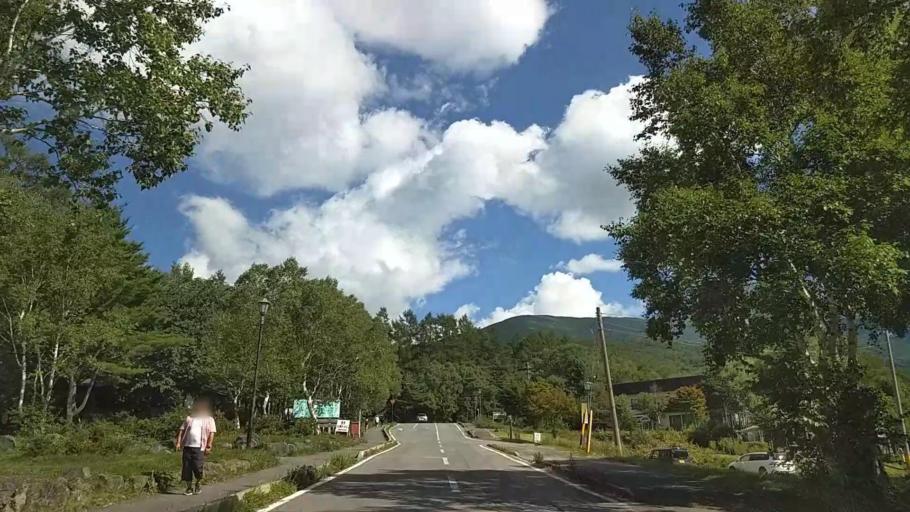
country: JP
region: Nagano
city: Chino
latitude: 36.1337
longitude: 138.2697
